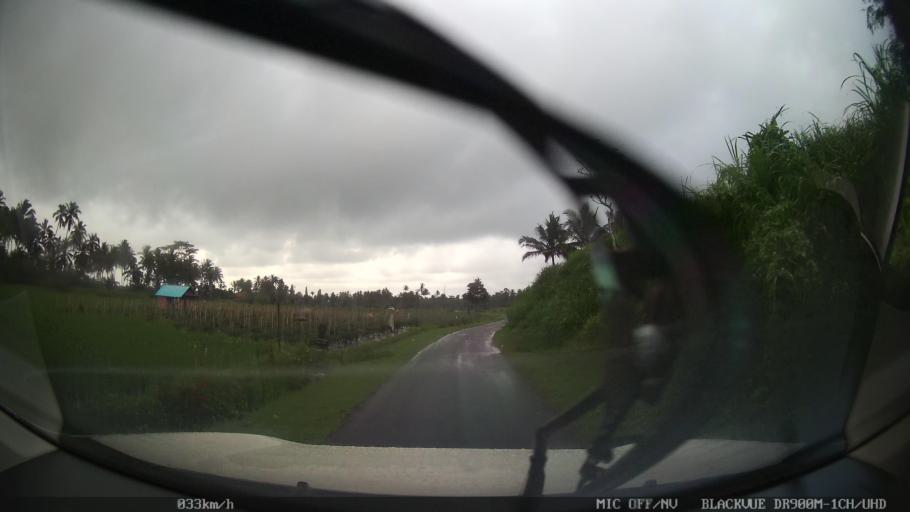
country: ID
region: Bali
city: Kekeran
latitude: -8.4814
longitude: 115.1873
